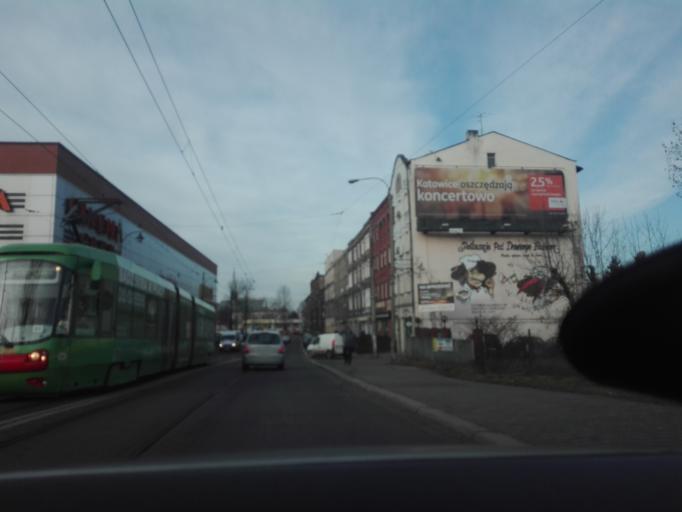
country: PL
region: Silesian Voivodeship
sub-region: Katowice
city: Katowice
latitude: 50.2626
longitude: 19.0073
